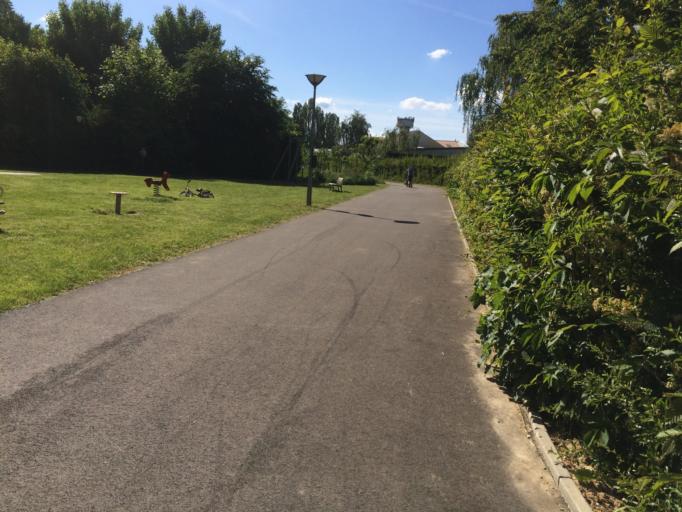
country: FR
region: Ile-de-France
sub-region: Departement de l'Essonne
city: Saclay
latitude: 48.7288
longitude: 2.1695
